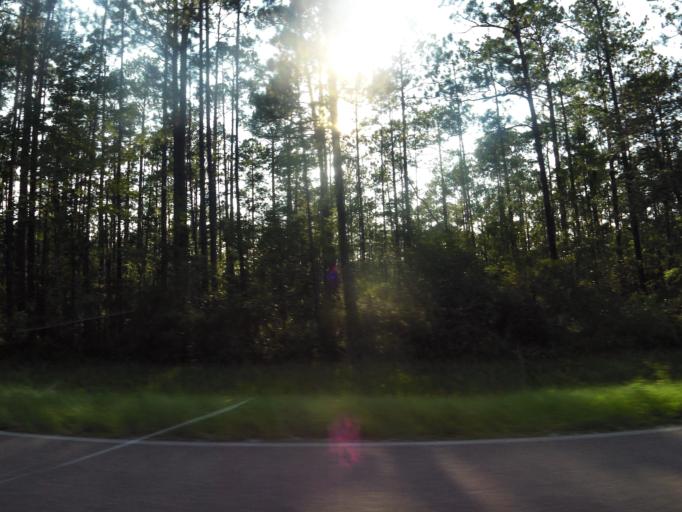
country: US
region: Florida
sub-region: Duval County
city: Baldwin
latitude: 30.3791
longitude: -82.0173
